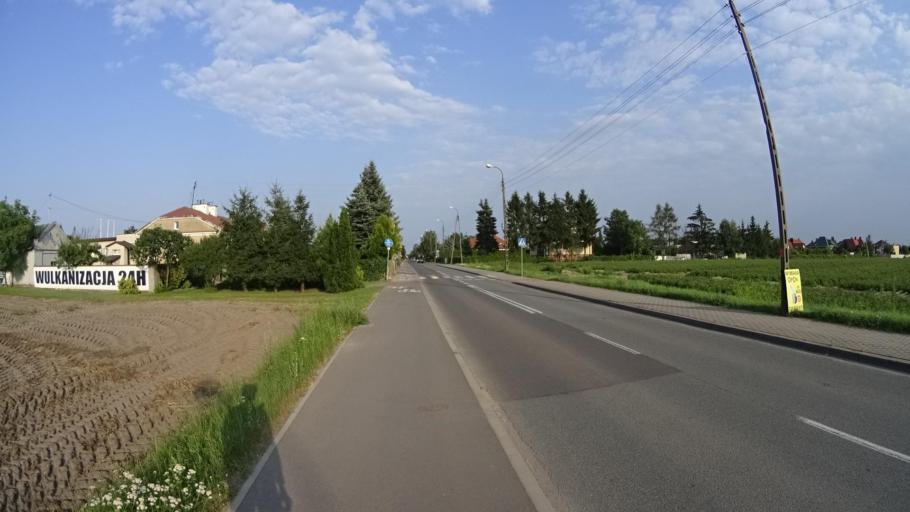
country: PL
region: Masovian Voivodeship
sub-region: Powiat pruszkowski
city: Rybie
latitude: 52.1491
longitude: 20.9395
